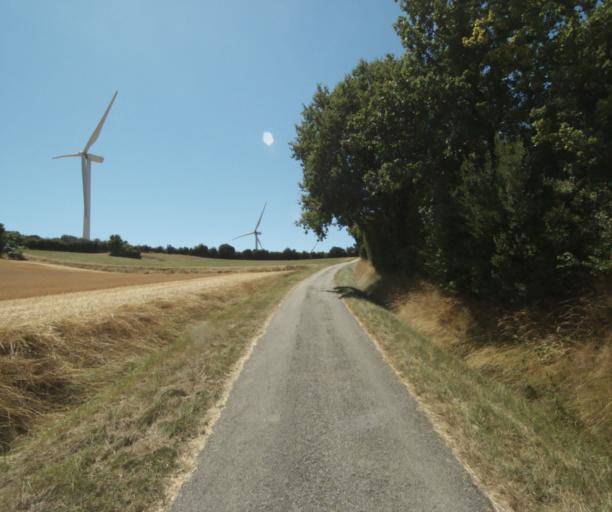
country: FR
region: Midi-Pyrenees
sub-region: Departement de la Haute-Garonne
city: Saint-Felix-Lauragais
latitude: 43.4638
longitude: 1.9212
